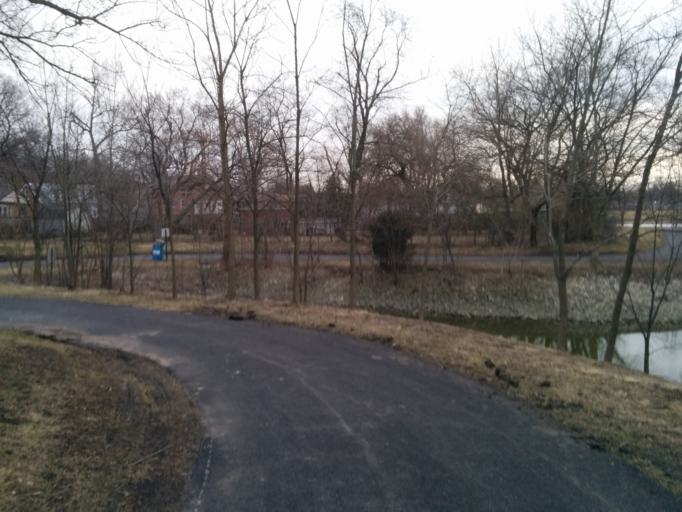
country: US
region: Illinois
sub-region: DuPage County
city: Villa Park
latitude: 41.8887
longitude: -87.9951
